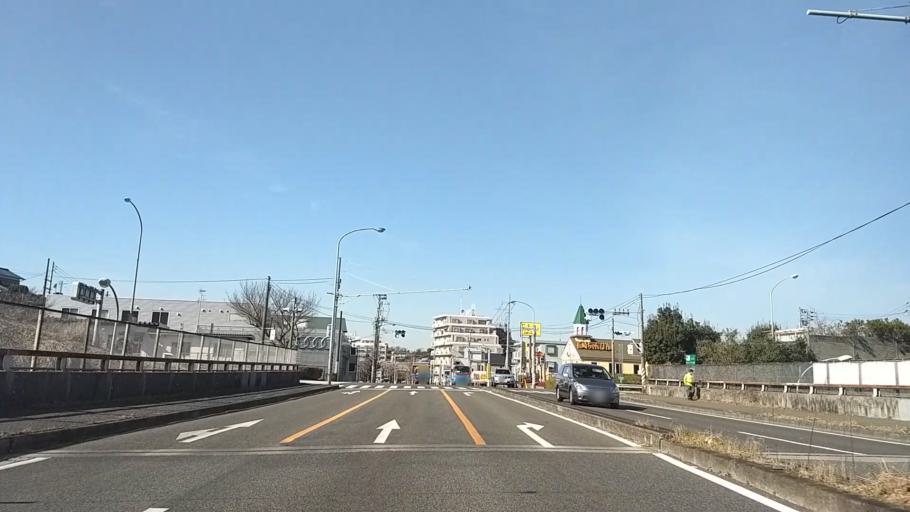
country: JP
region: Kanagawa
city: Kamakura
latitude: 35.3699
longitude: 139.5949
